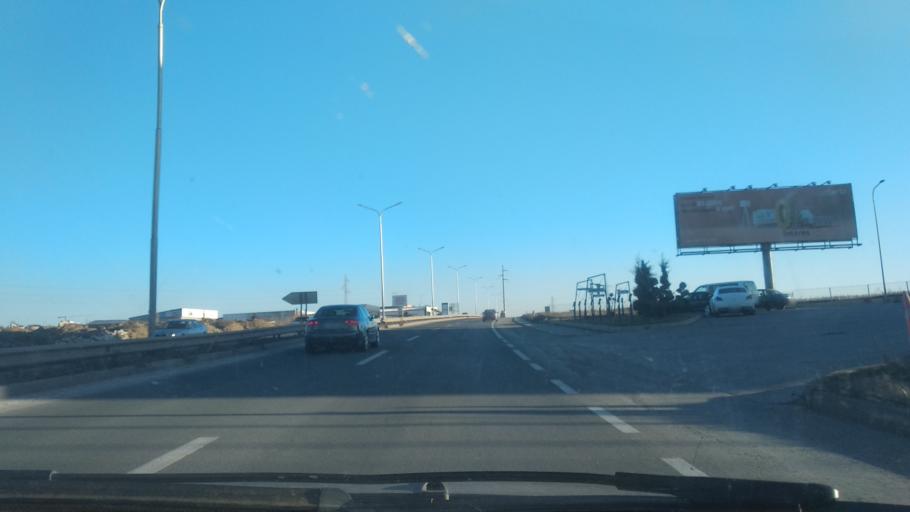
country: XK
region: Pristina
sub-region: Kosovo Polje
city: Kosovo Polje
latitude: 42.6655
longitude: 21.1264
